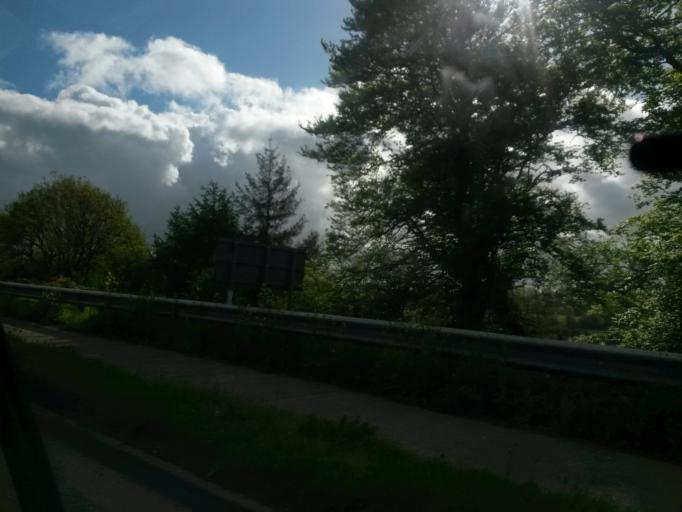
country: IE
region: Leinster
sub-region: Loch Garman
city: Enniscorthy
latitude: 52.5106
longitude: -6.5649
